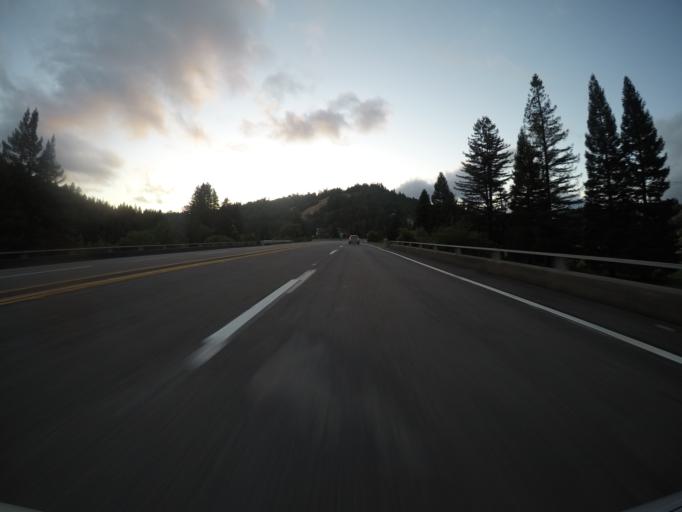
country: US
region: California
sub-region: Humboldt County
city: Redway
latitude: 40.0652
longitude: -123.7859
